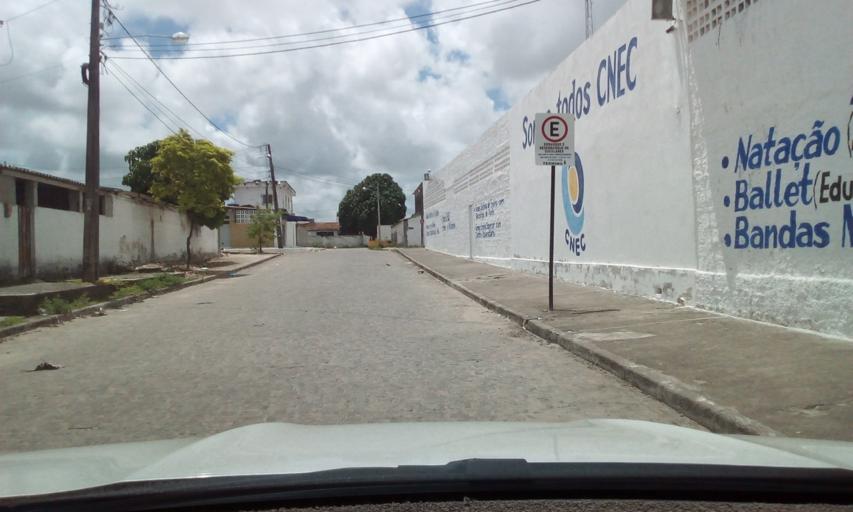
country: BR
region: Paraiba
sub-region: Joao Pessoa
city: Joao Pessoa
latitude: -7.1773
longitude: -34.8667
